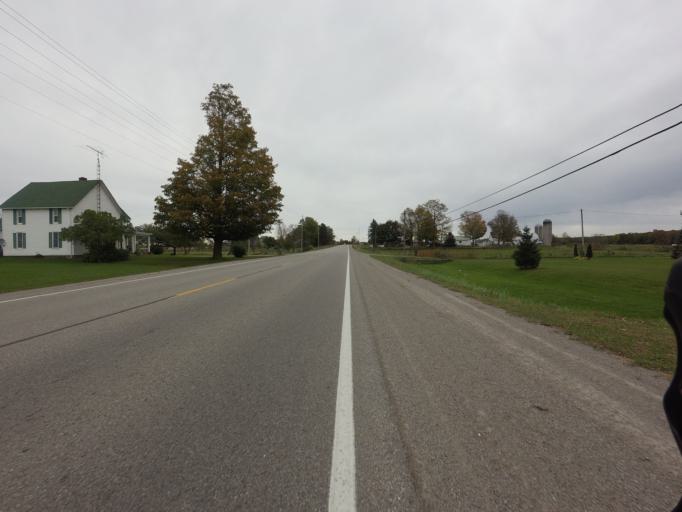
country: CA
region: Ontario
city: Brockville
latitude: 44.6319
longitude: -75.9373
